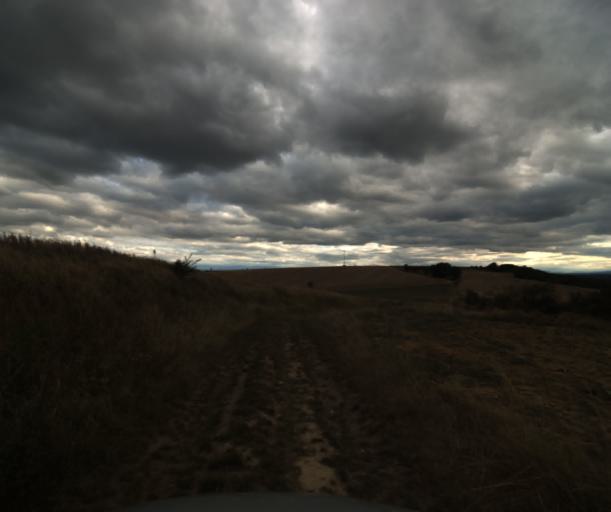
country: FR
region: Midi-Pyrenees
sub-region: Departement de la Haute-Garonne
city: Le Fauga
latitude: 43.3975
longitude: 1.3119
